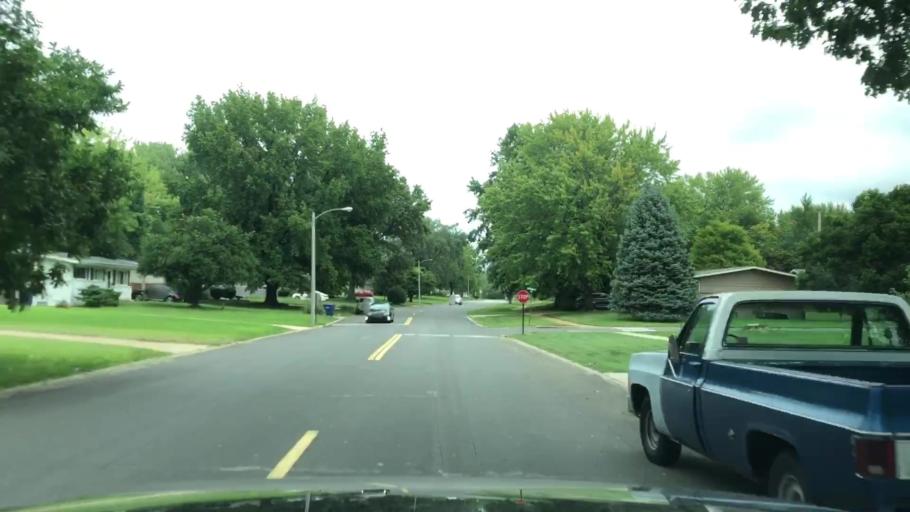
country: US
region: Missouri
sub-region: Saint Louis County
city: Florissant
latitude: 38.8041
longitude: -90.3152
